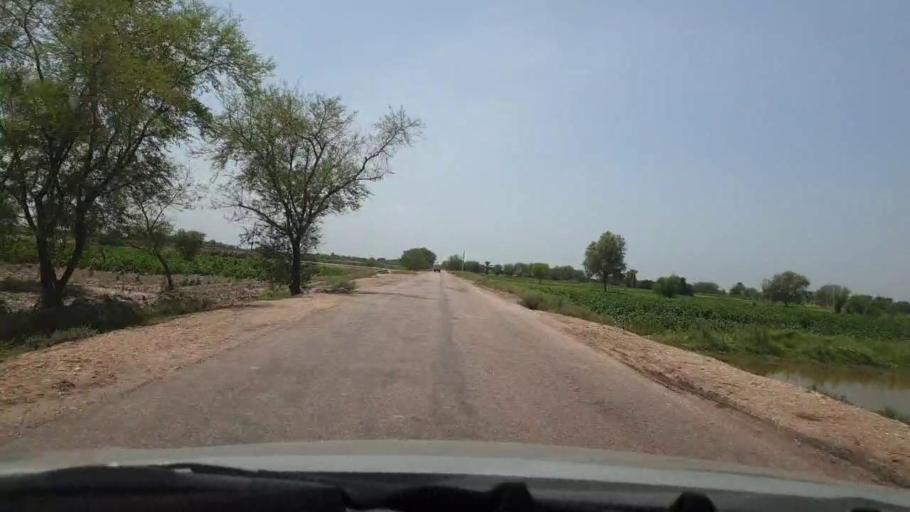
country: PK
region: Sindh
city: Pano Aqil
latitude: 27.6634
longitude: 69.1506
